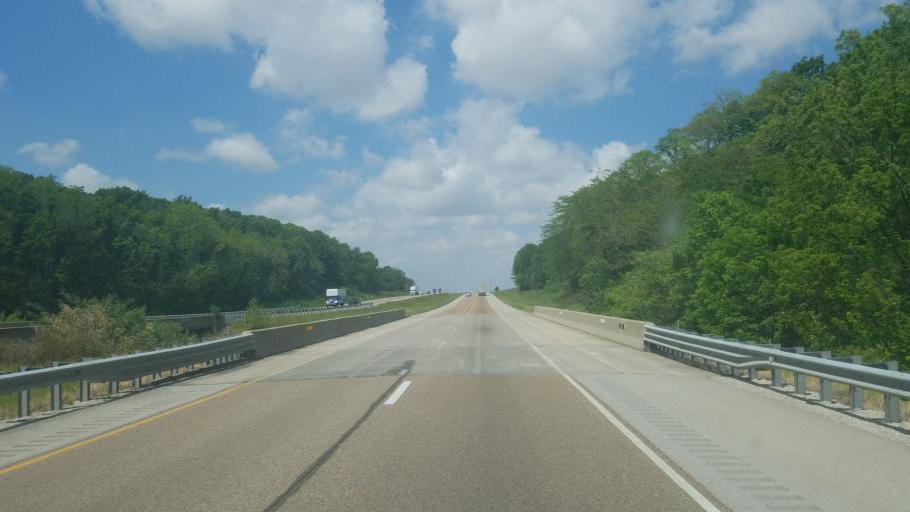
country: US
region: Illinois
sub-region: Clark County
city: Casey
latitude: 39.2826
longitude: -88.0627
